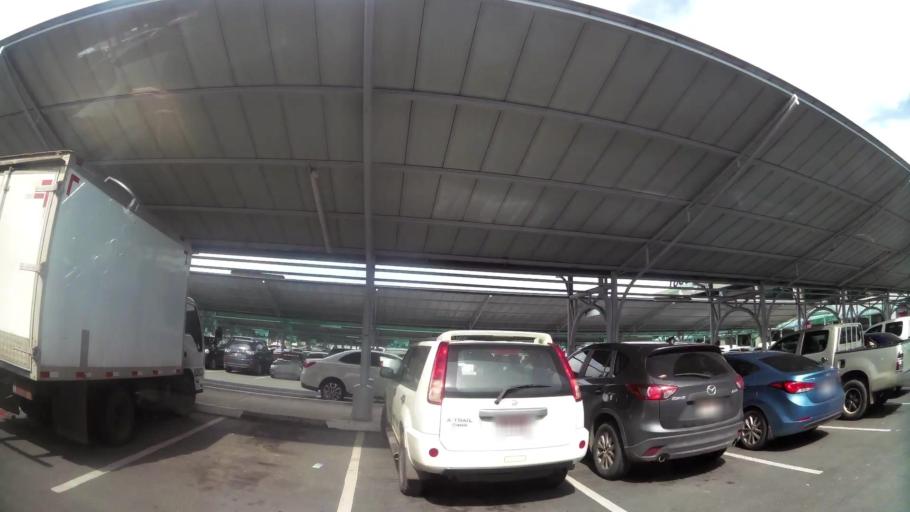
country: PA
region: Panama
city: Tocumen
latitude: 9.0669
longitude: -79.3884
